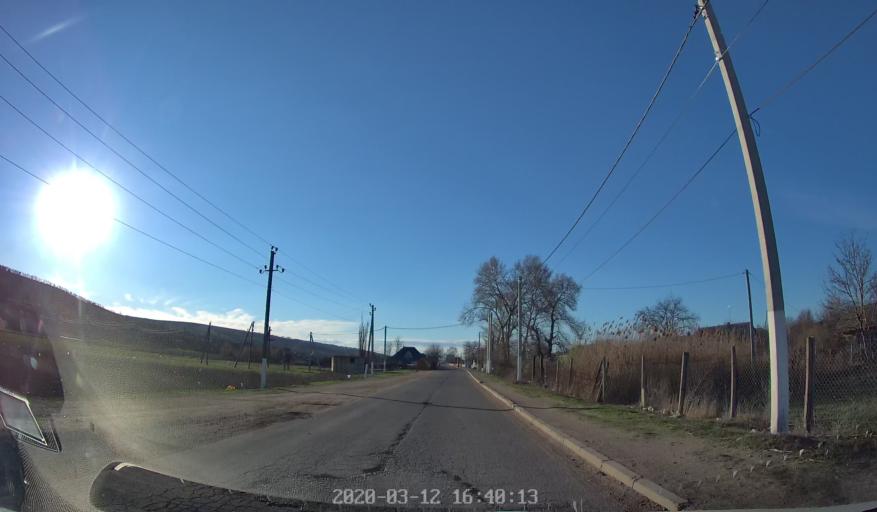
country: MD
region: Anenii Noi
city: Anenii Noi
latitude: 46.8171
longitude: 29.1509
